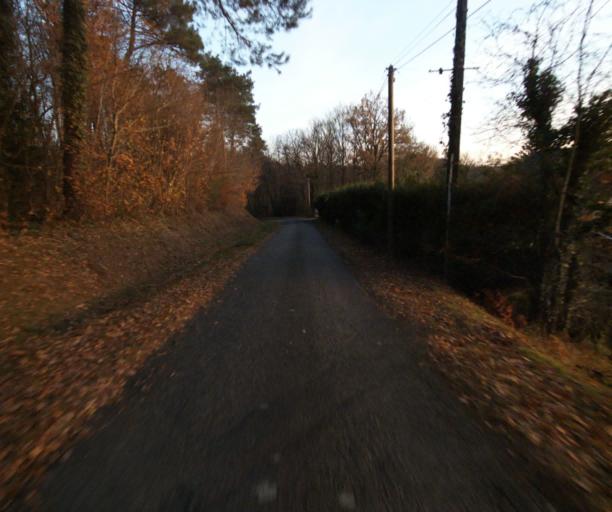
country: FR
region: Limousin
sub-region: Departement de la Correze
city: Laguenne
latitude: 45.2213
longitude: 1.8224
